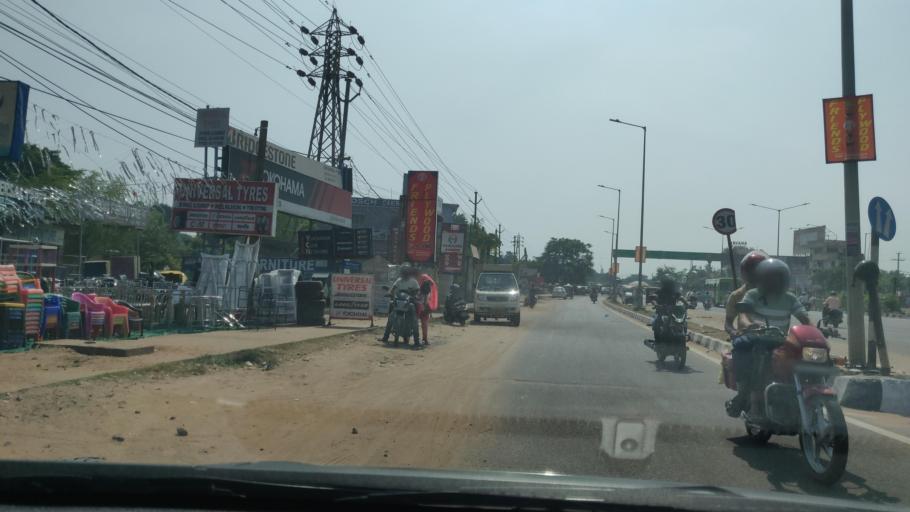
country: IN
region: Odisha
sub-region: Khordha
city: Bhubaneshwar
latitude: 20.2503
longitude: 85.7844
